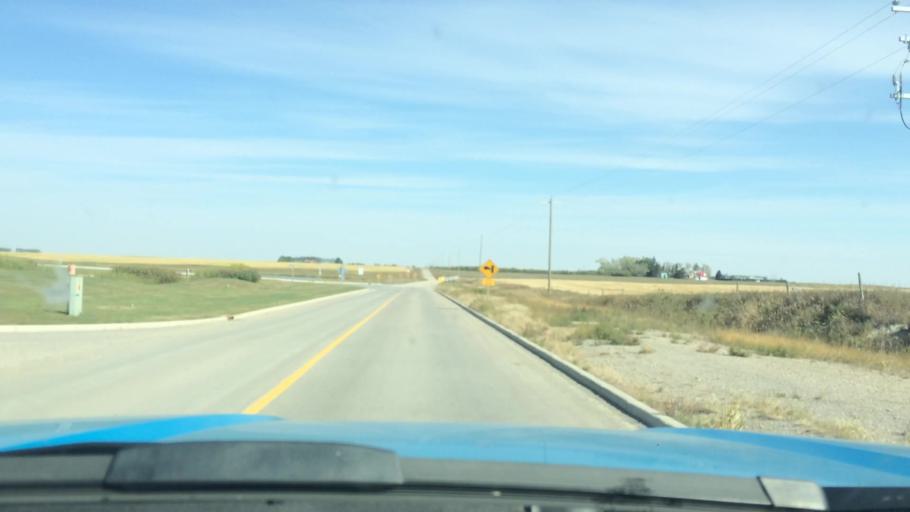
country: CA
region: Alberta
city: Airdrie
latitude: 51.2161
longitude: -113.9352
